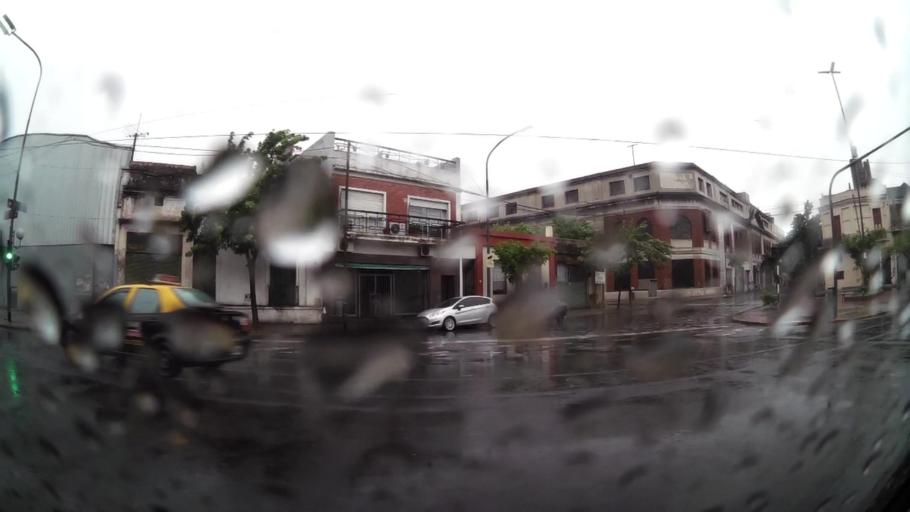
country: AR
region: Buenos Aires F.D.
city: Buenos Aires
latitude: -34.6392
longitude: -58.3882
